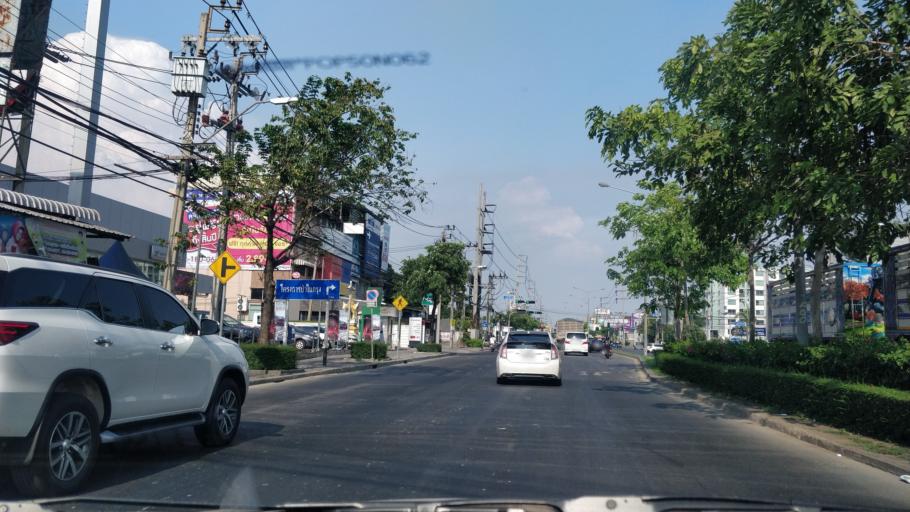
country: TH
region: Bangkok
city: Suan Luang
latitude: 13.7216
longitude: 100.7017
